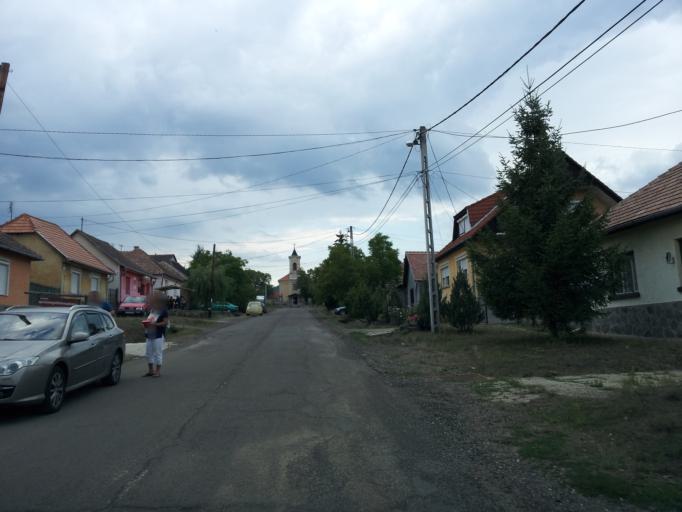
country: HU
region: Pest
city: Kismaros
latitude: 47.8768
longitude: 18.9339
